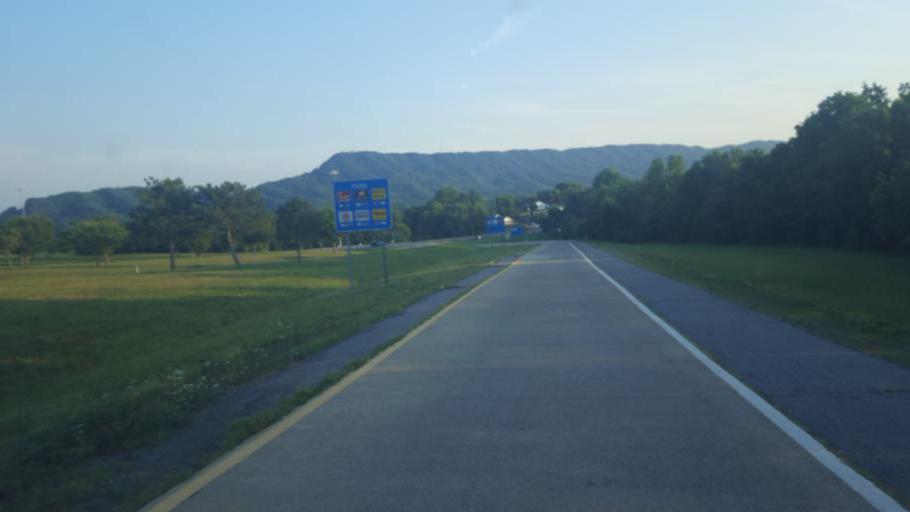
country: US
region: Tennessee
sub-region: Sullivan County
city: Kingsport
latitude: 36.5589
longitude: -82.5839
